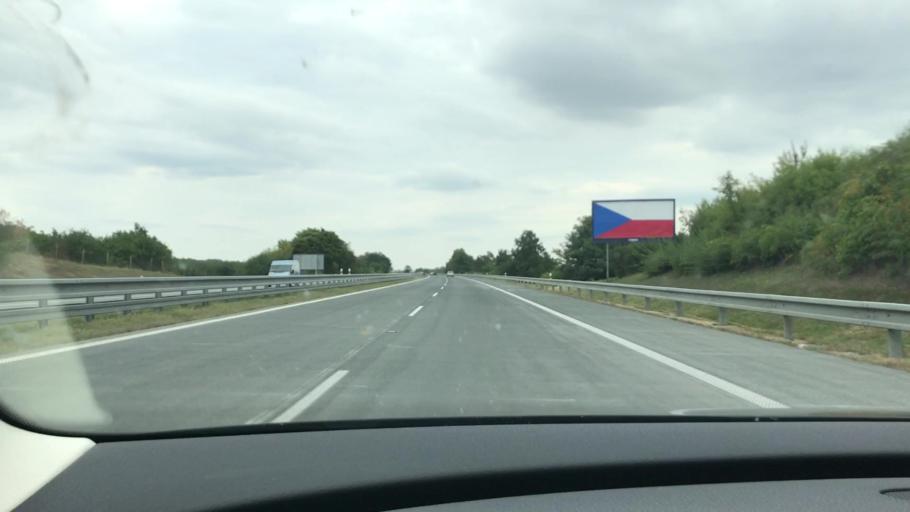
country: CZ
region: South Moravian
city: Velke Nemcice
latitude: 48.9817
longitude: 16.6958
